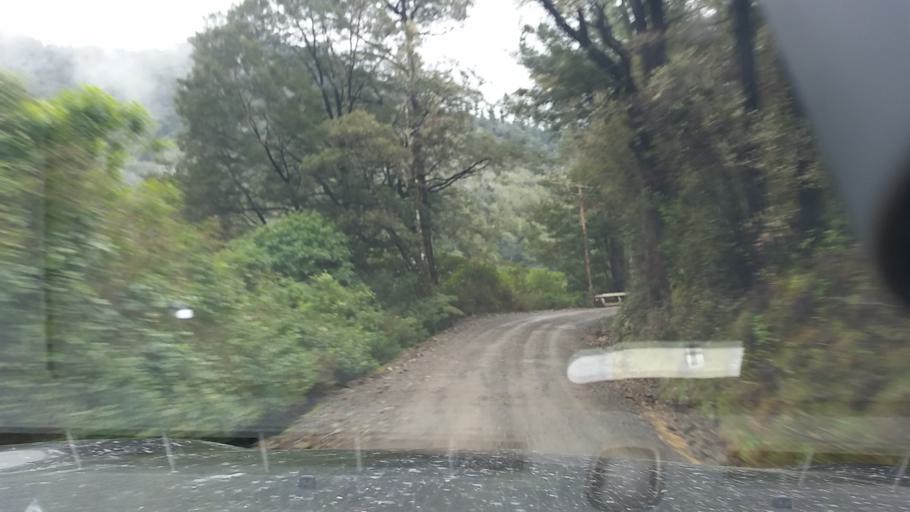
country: NZ
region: Nelson
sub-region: Nelson City
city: Nelson
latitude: -41.3581
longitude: 173.6210
